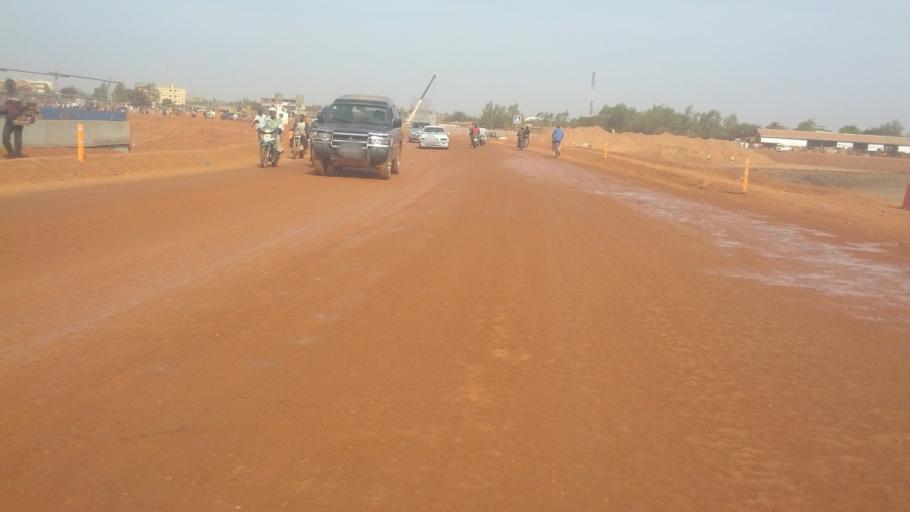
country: BF
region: Centre
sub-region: Kadiogo Province
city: Ouagadougou
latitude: 12.3830
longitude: -1.5562
